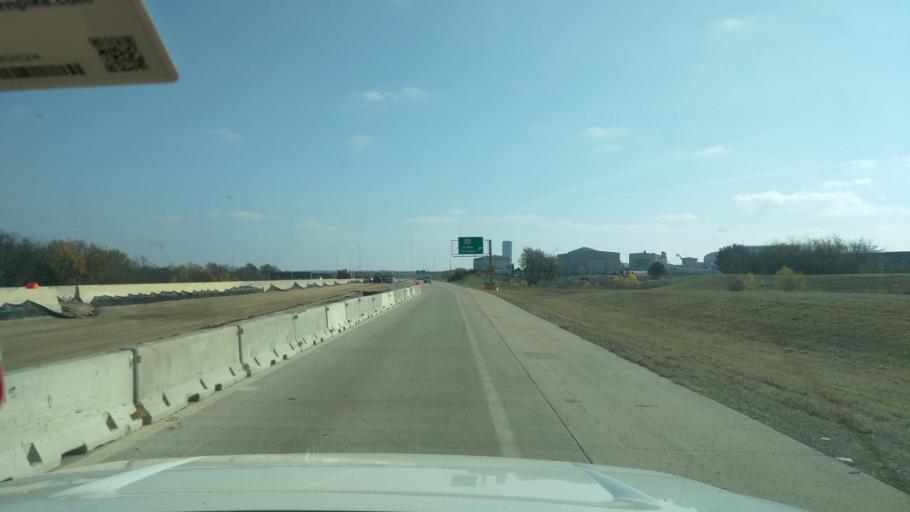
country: US
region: Oklahoma
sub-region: Tulsa County
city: Broken Arrow
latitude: 36.0504
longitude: -95.7519
